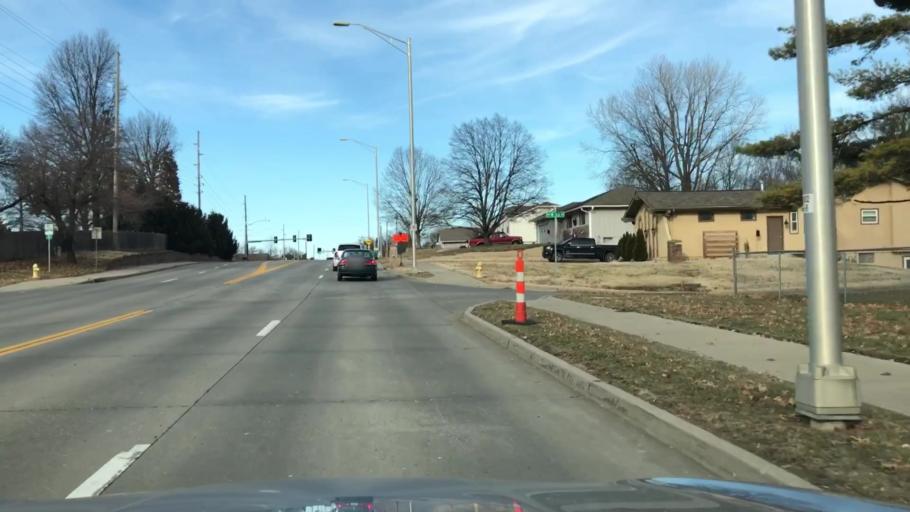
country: US
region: Missouri
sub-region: Jackson County
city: Lees Summit
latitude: 38.9103
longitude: -94.4136
